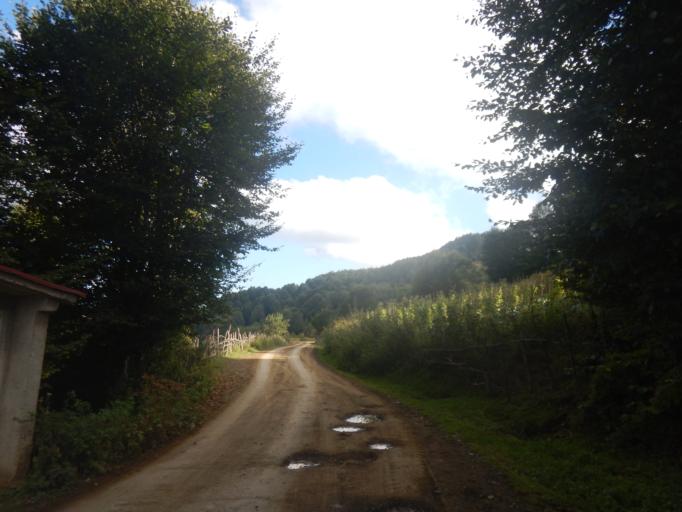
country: TR
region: Ordu
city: Golkoy
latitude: 40.6535
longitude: 37.5503
